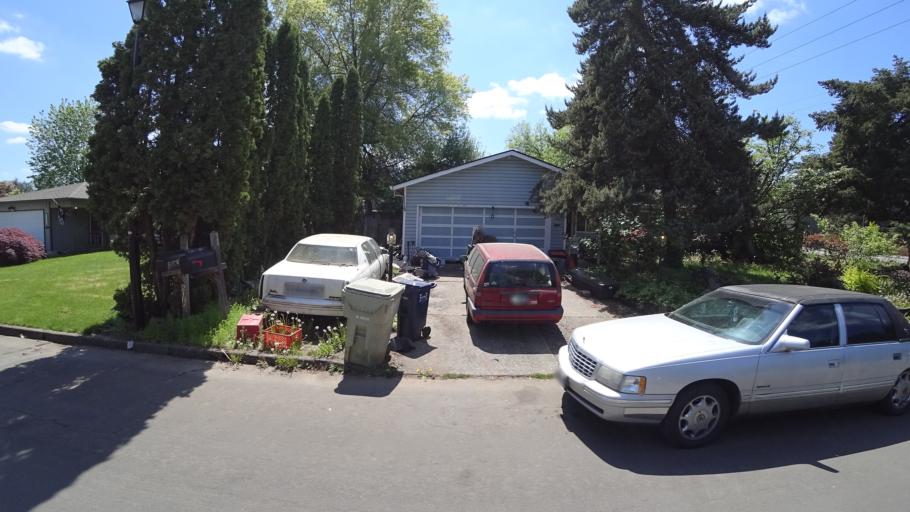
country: US
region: Oregon
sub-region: Washington County
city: Aloha
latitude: 45.5049
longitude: -122.9017
